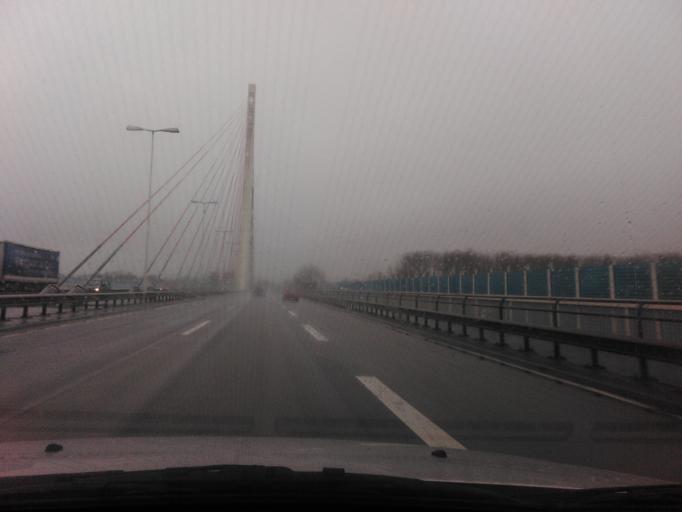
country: DE
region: Rheinland-Pfalz
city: Weissenthurm
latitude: 50.4201
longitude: 7.4554
